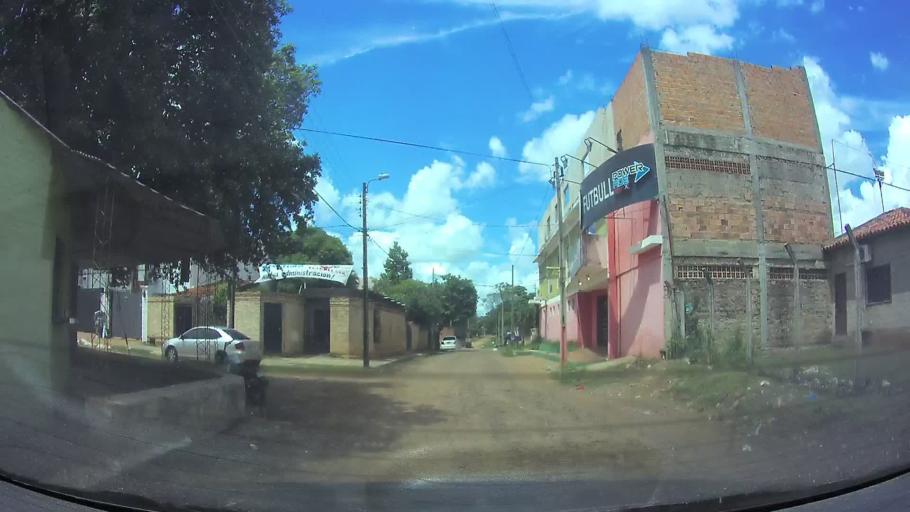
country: PY
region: Central
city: Fernando de la Mora
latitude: -25.3150
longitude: -57.5247
